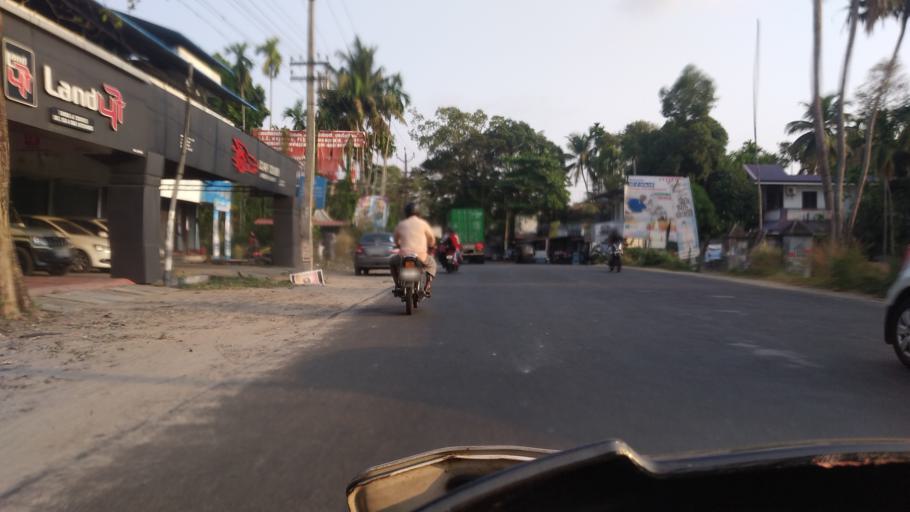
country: IN
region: Kerala
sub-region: Thrissur District
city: Irinjalakuda
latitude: 10.3362
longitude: 76.1387
